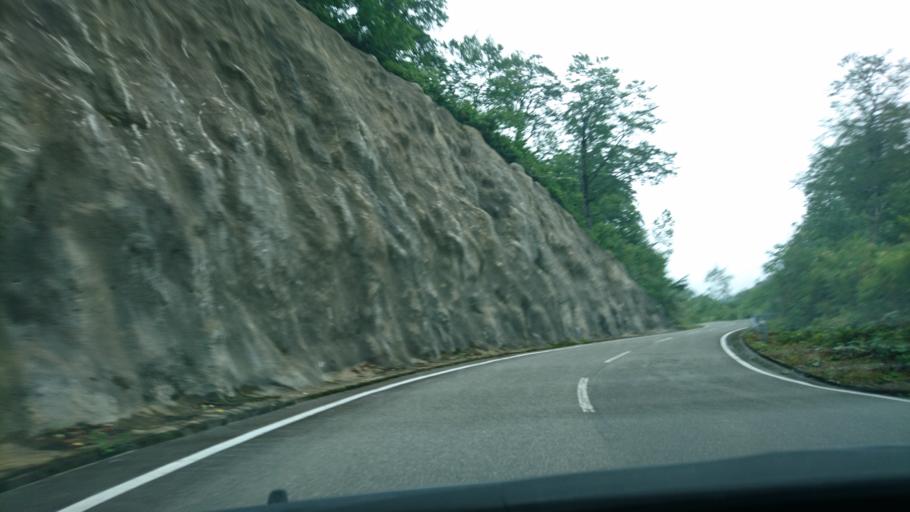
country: JP
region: Akita
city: Yuzawa
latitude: 38.9798
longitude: 140.7437
